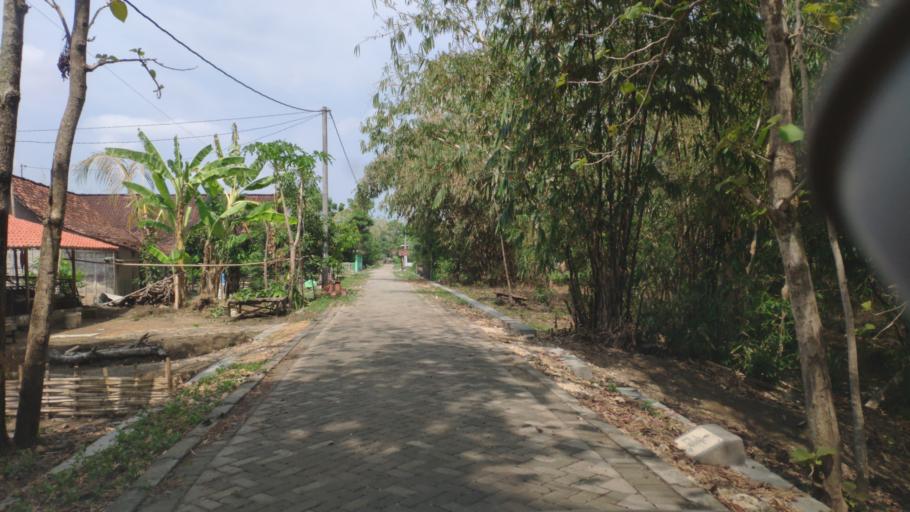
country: ID
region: Central Java
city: Karangtalun
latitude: -7.0193
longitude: 111.3589
